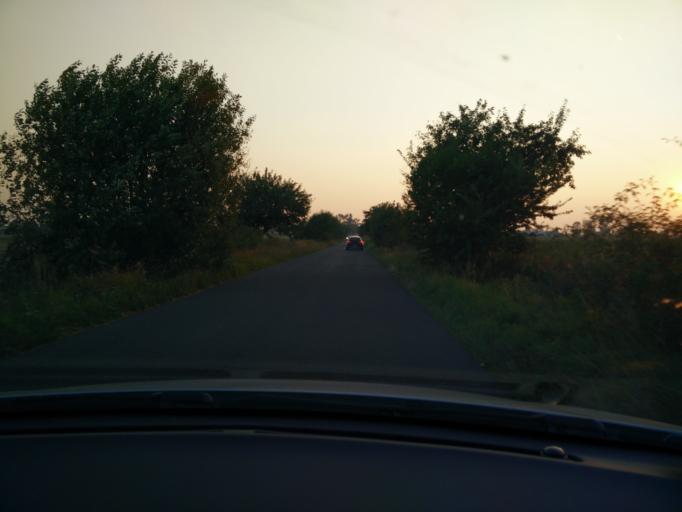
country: PL
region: Greater Poland Voivodeship
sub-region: Powiat wrzesinski
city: Miloslaw
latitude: 52.2451
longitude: 17.5309
